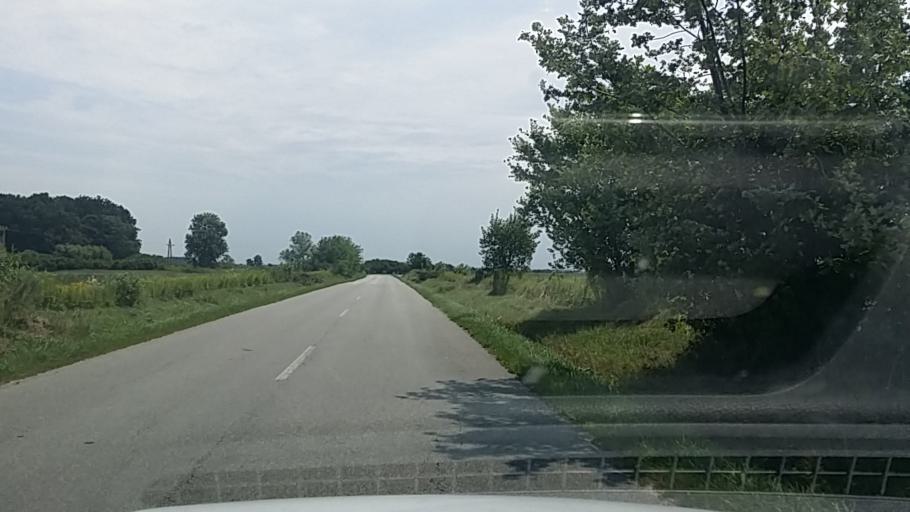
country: HU
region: Zala
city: Becsehely
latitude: 46.4162
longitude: 16.7736
